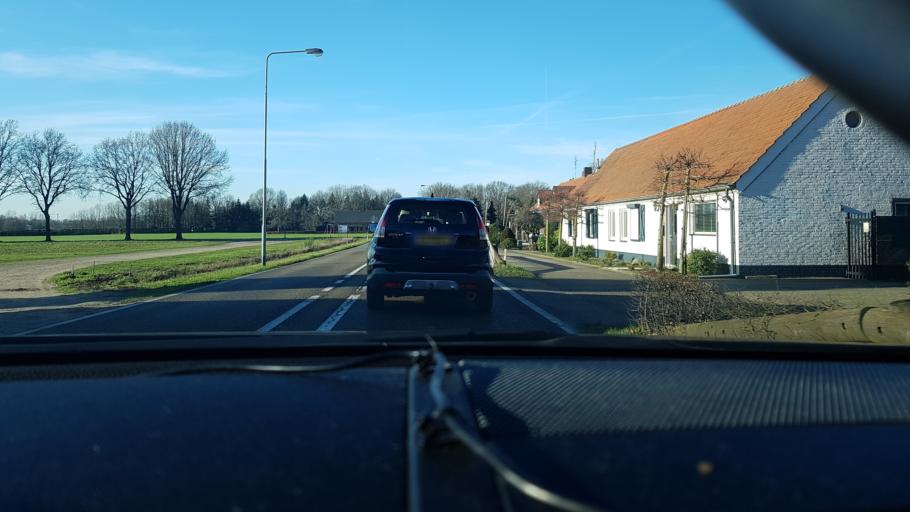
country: NL
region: Limburg
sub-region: Gemeente Leudal
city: Heythuysen
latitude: 51.3430
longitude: 5.9090
